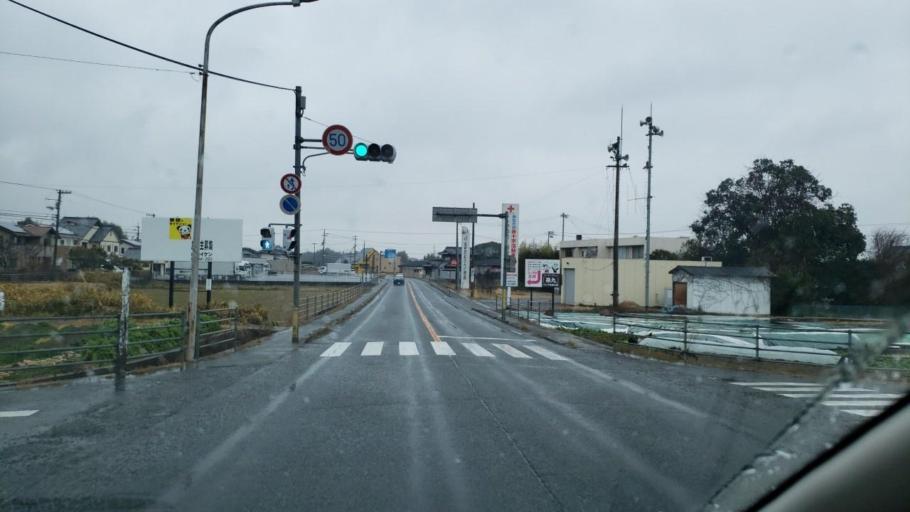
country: JP
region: Tokushima
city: Narutocho-mitsuishi
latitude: 34.1556
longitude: 134.5291
